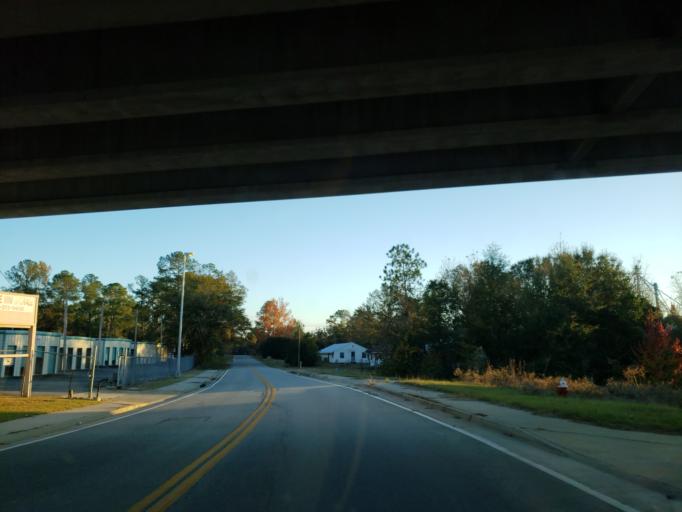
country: US
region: Georgia
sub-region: Crisp County
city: Cordele
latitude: 31.9551
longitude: -83.7793
